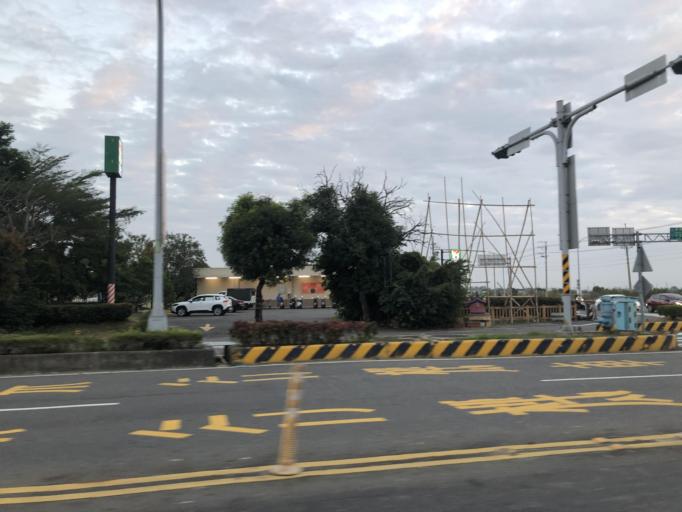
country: TW
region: Taiwan
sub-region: Tainan
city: Tainan
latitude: 23.0238
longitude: 120.3092
